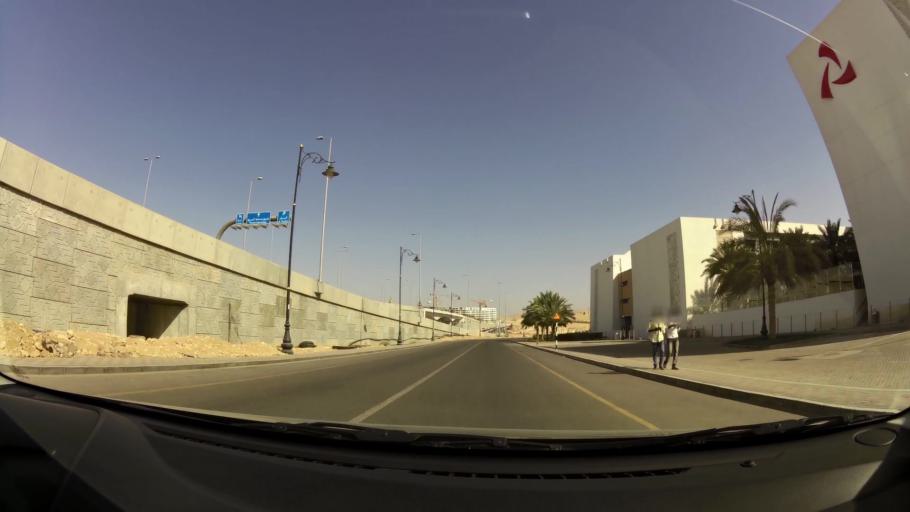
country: OM
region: Muhafazat Masqat
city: Bawshar
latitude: 23.5800
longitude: 58.2937
